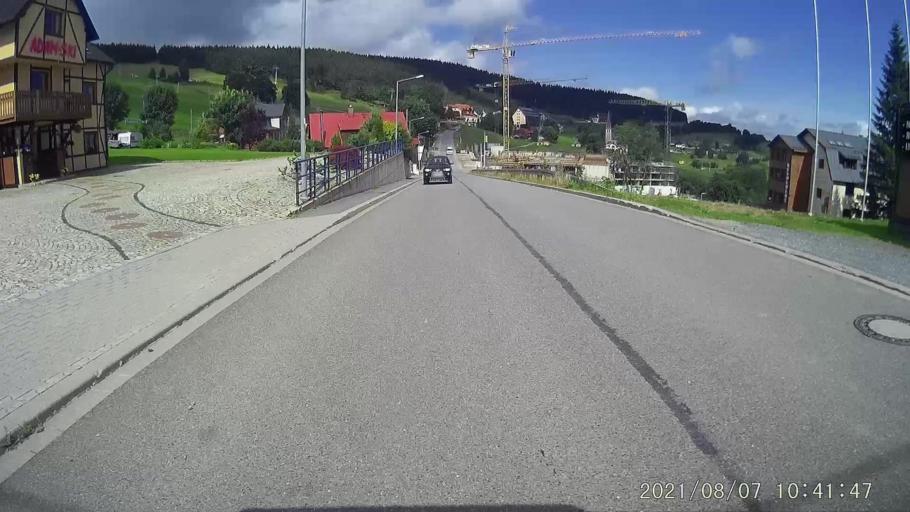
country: PL
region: Lower Silesian Voivodeship
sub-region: Powiat klodzki
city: Duszniki-Zdroj
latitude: 50.3360
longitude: 16.3881
